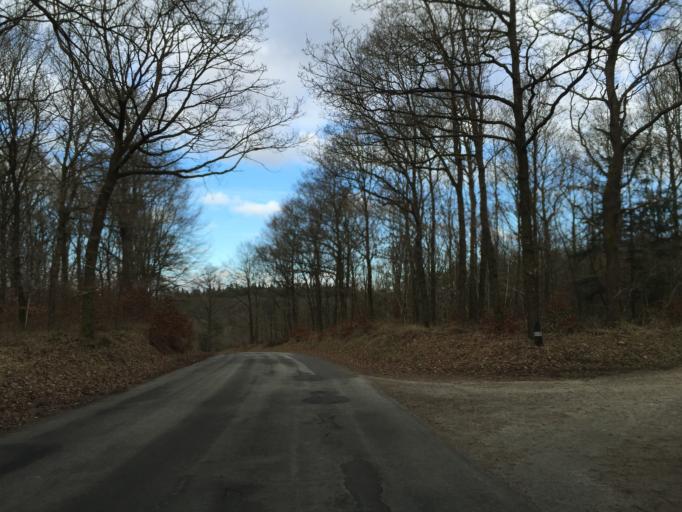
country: DK
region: Central Jutland
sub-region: Viborg Kommune
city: Viborg
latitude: 56.3786
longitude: 9.3336
